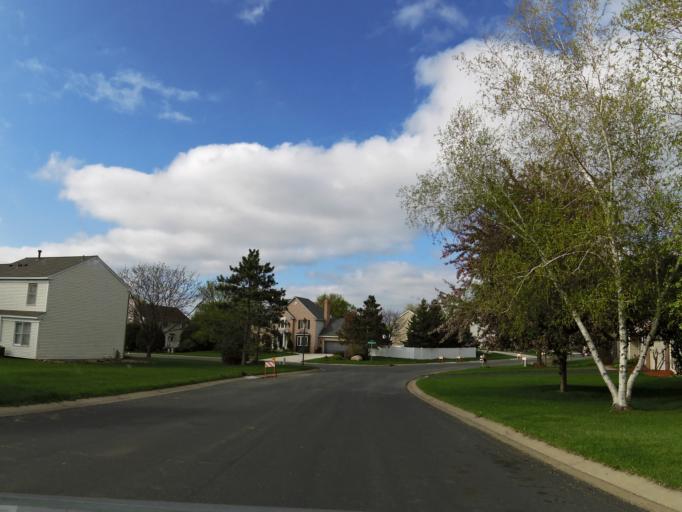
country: US
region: Minnesota
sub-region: Washington County
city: Woodbury
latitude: 44.9207
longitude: -92.9211
